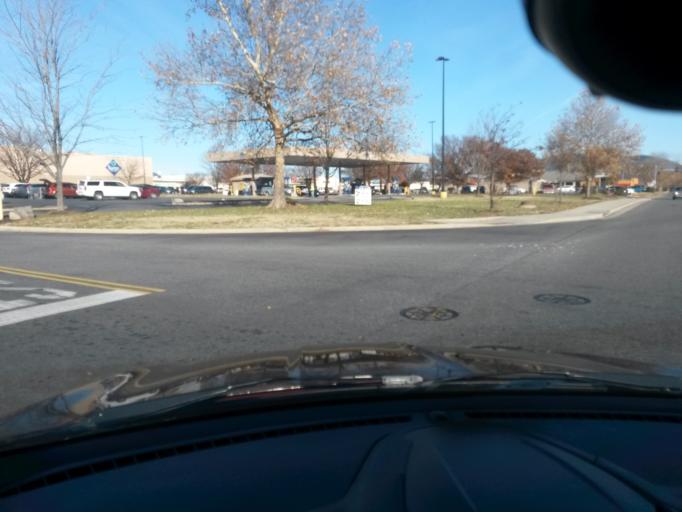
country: US
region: Virginia
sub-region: Roanoke County
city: Hollins
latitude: 37.3182
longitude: -79.9661
